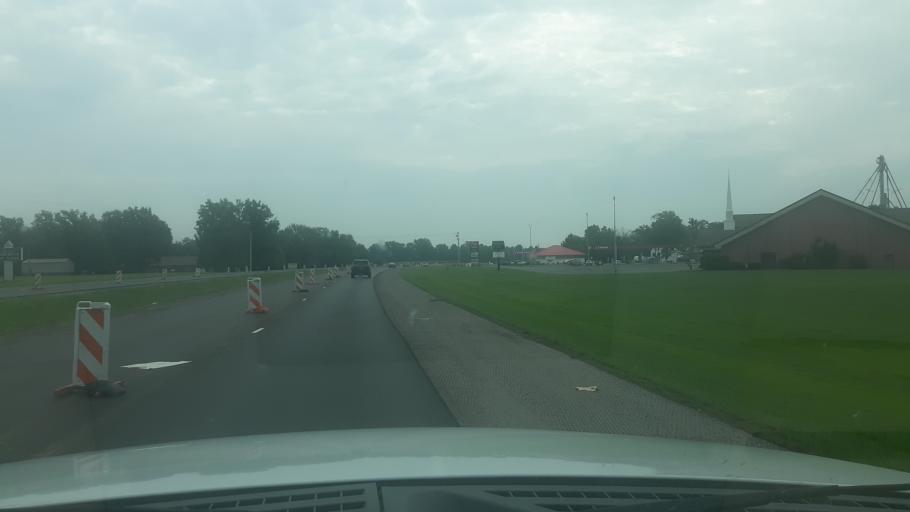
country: US
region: Illinois
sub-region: Williamson County
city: Marion
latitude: 37.7397
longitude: -88.9063
